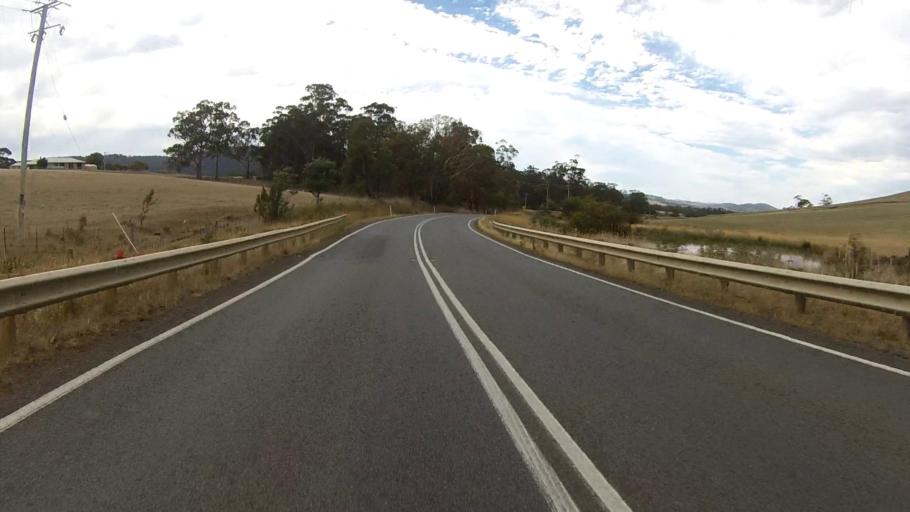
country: AU
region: Tasmania
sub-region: Sorell
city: Sorell
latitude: -42.7079
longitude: 147.5045
